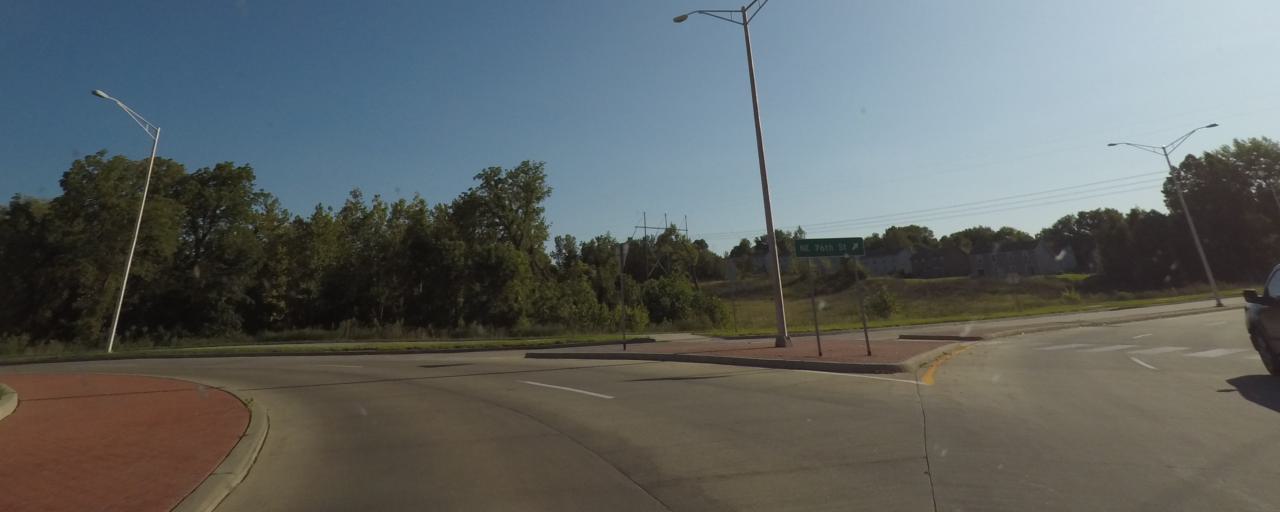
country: US
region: Missouri
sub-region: Clay County
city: Pleasant Valley
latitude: 39.2310
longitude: -94.4704
